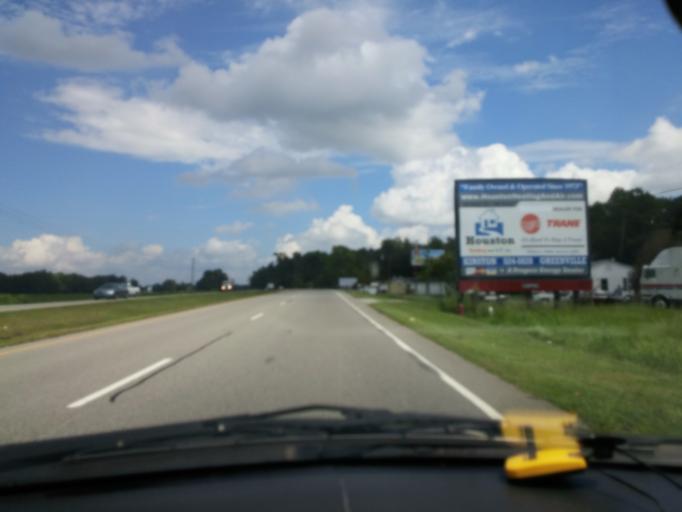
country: US
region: North Carolina
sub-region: Pitt County
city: Grifton
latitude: 35.3474
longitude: -77.4704
